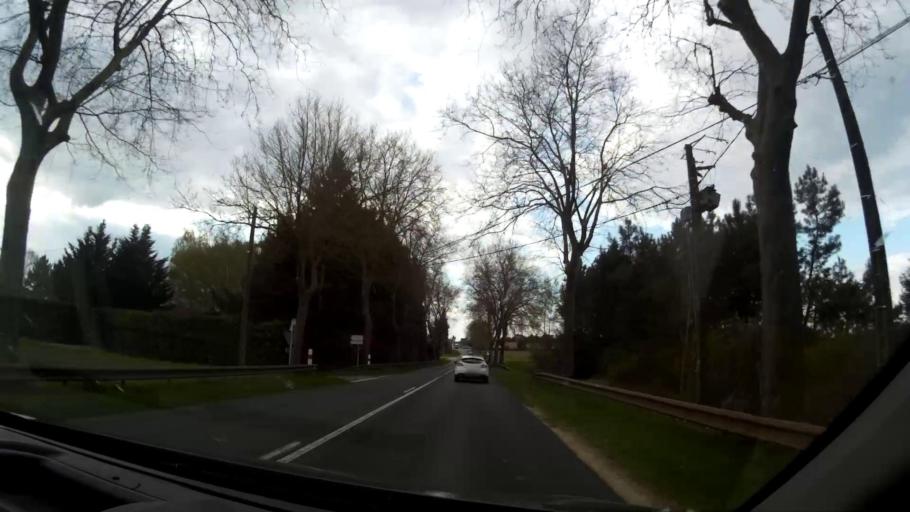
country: FR
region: Centre
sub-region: Departement du Loir-et-Cher
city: Cormeray
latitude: 47.4834
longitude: 1.4127
